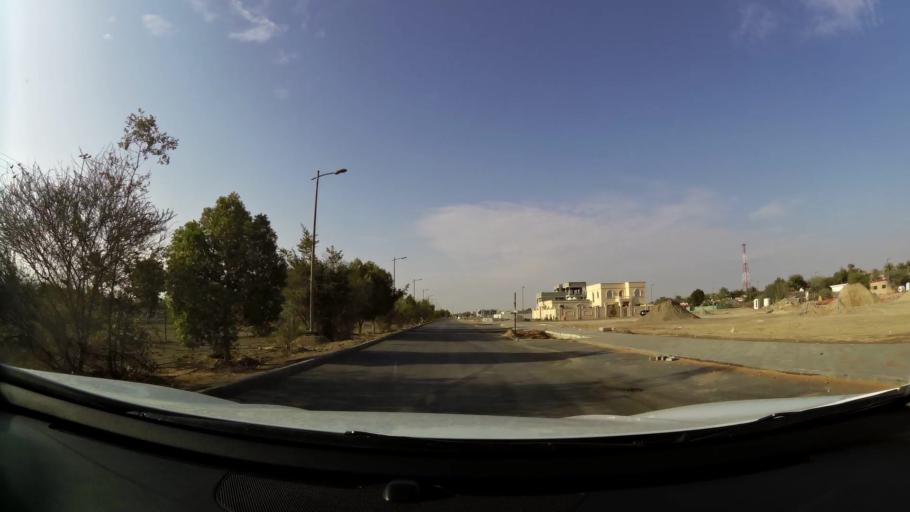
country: AE
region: Abu Dhabi
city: Al Ain
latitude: 24.0808
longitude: 55.8338
